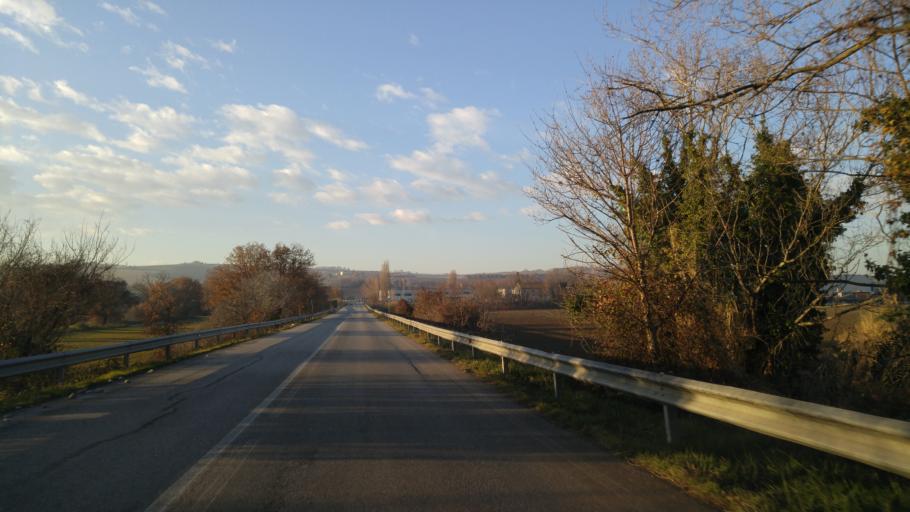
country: IT
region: The Marches
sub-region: Provincia di Ancona
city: Monterado
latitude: 43.7064
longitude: 13.0806
